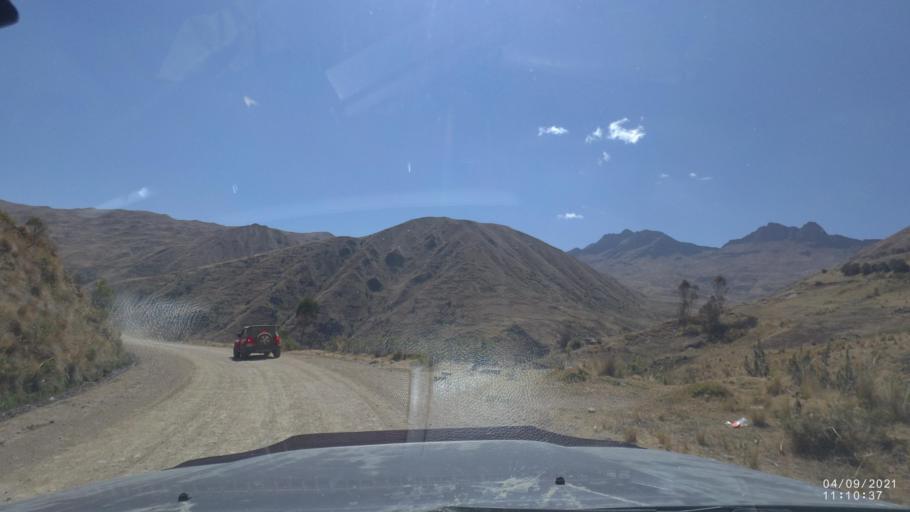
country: BO
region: Cochabamba
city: Sipe Sipe
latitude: -17.2781
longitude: -66.4821
